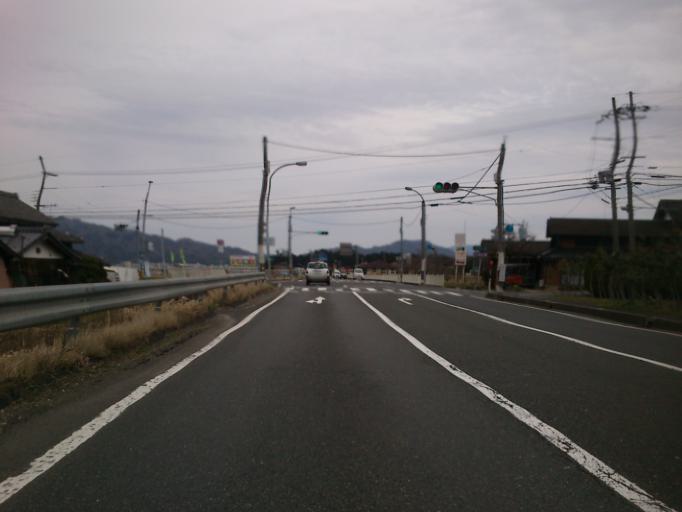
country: JP
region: Kyoto
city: Miyazu
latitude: 35.5005
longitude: 135.1028
